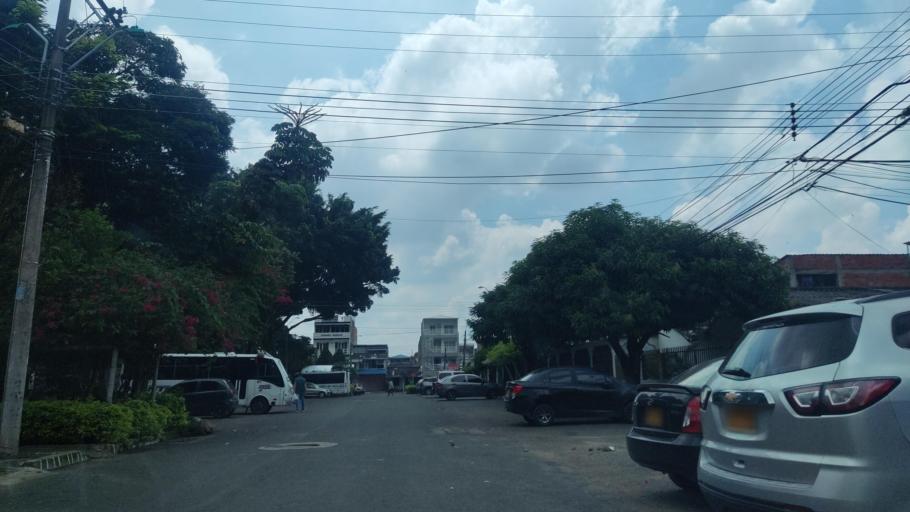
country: CO
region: Valle del Cauca
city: Cali
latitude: 3.4003
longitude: -76.5017
